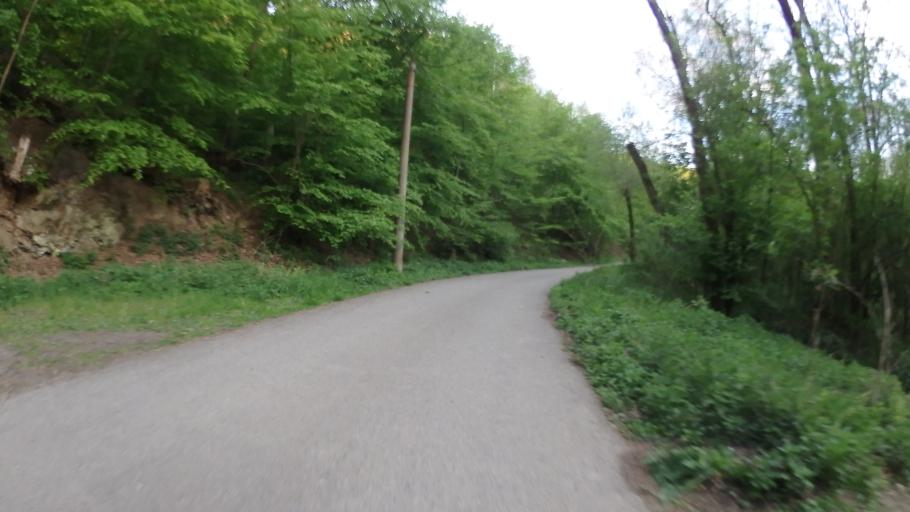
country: CZ
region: South Moravian
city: Strelice
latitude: 49.1401
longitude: 16.4780
